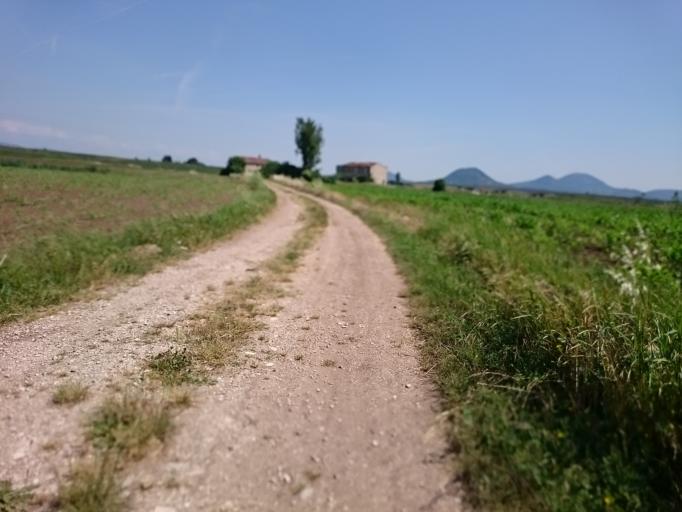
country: IT
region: Veneto
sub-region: Provincia di Padova
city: Saletto
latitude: 45.2541
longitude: 11.5616
